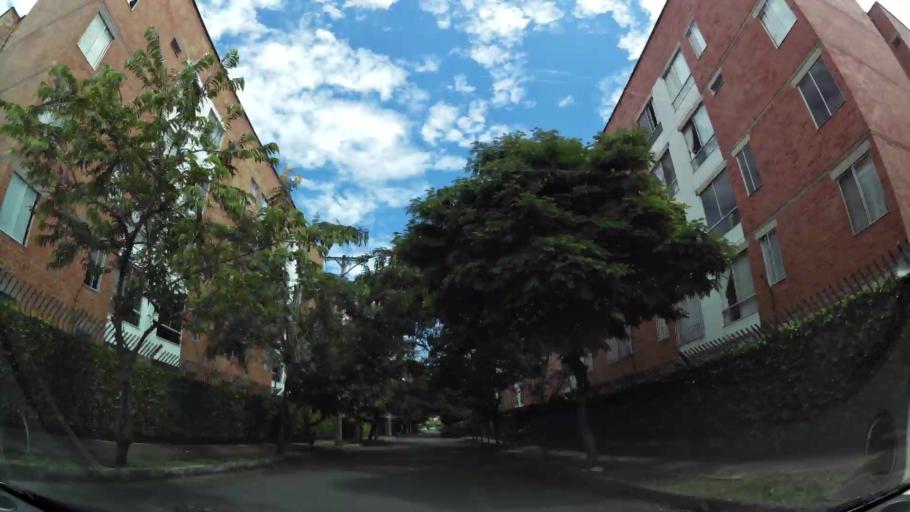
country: CO
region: Valle del Cauca
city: Cali
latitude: 3.3731
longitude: -76.5201
